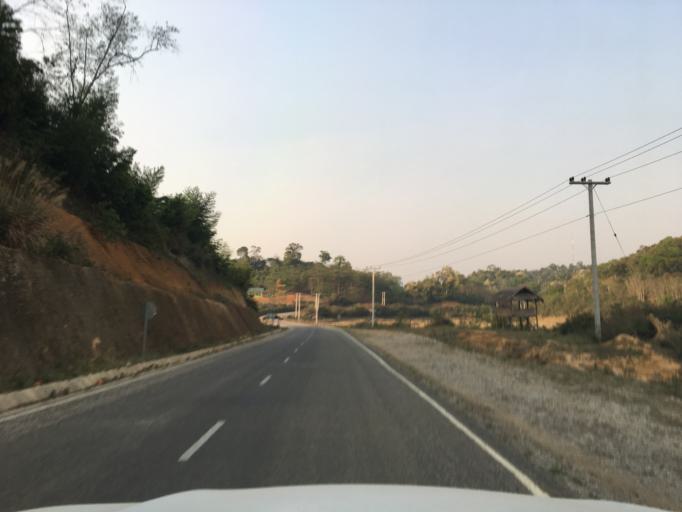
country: LA
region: Houaphan
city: Xam Nua
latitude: 20.5996
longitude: 104.0688
